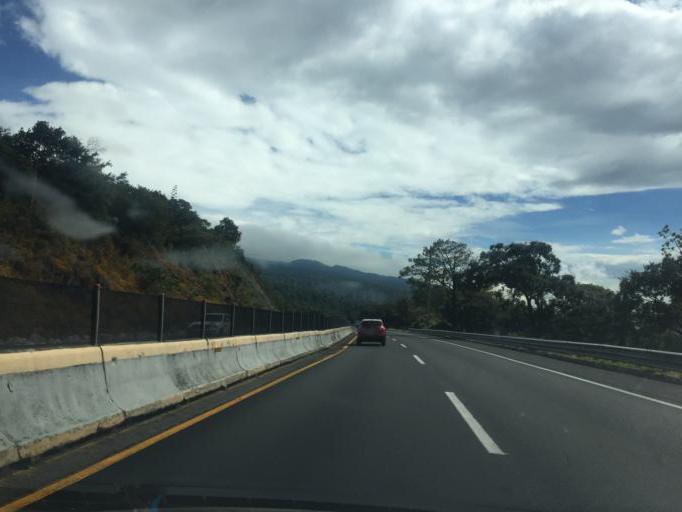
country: MX
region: Morelos
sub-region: Cuernavaca
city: Villa Santiago
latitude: 19.0248
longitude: -99.1891
